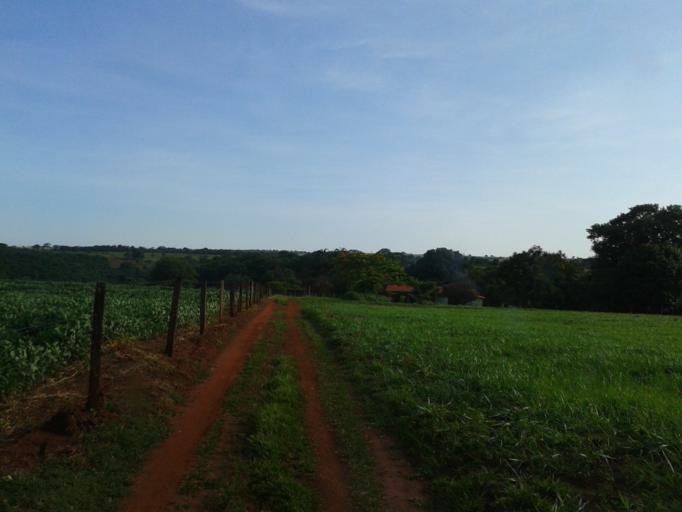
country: BR
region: Minas Gerais
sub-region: Centralina
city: Centralina
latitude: -18.7128
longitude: -49.1888
